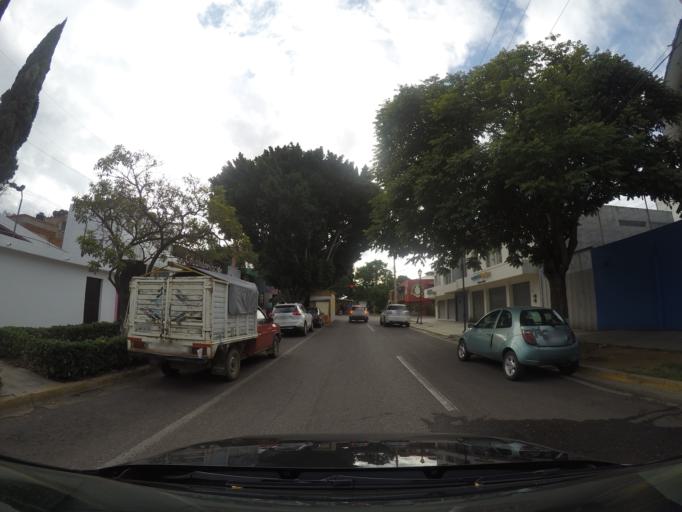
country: MX
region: Oaxaca
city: Oaxaca de Juarez
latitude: 17.0765
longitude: -96.7164
